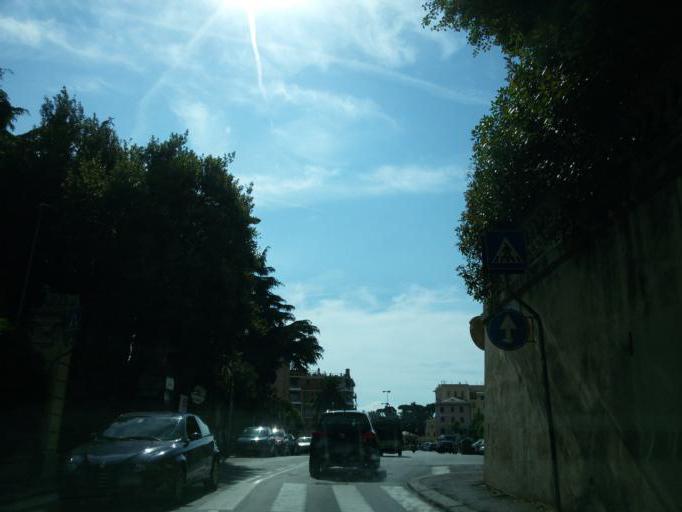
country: IT
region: Liguria
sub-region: Provincia di Genova
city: Genoa
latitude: 44.3958
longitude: 8.9741
